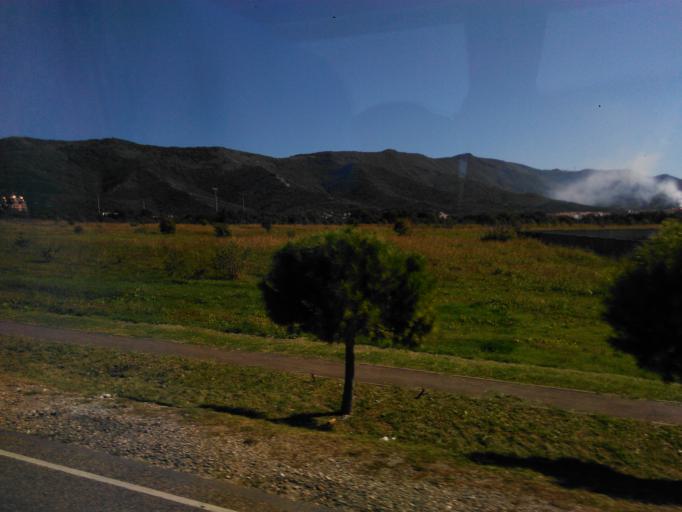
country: RU
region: Krasnodarskiy
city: Gelendzhik
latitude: 44.5949
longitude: 38.0271
